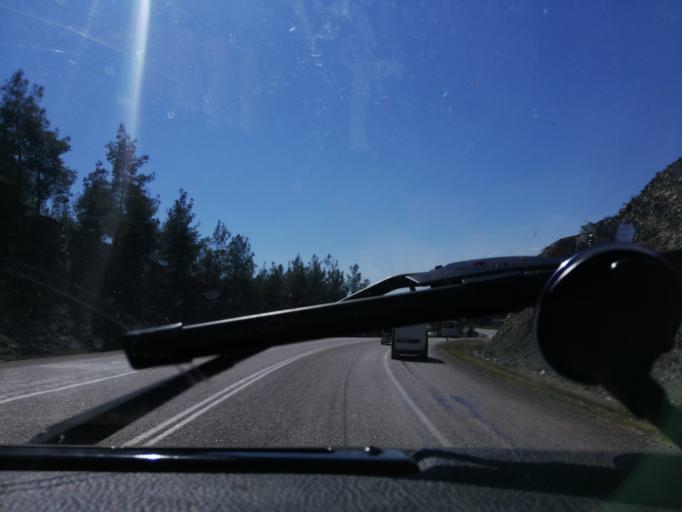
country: TR
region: Mugla
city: Kemer
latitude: 36.6089
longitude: 29.3584
